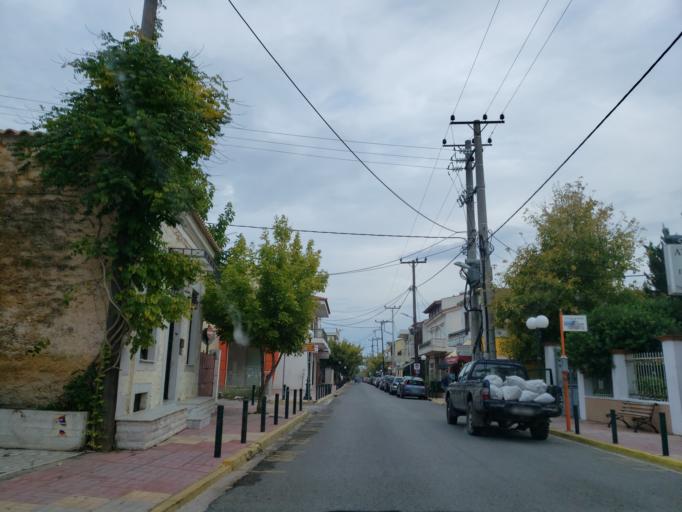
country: GR
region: Attica
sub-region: Nomarchia Anatolikis Attikis
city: Marathonas
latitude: 38.1560
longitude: 23.9602
